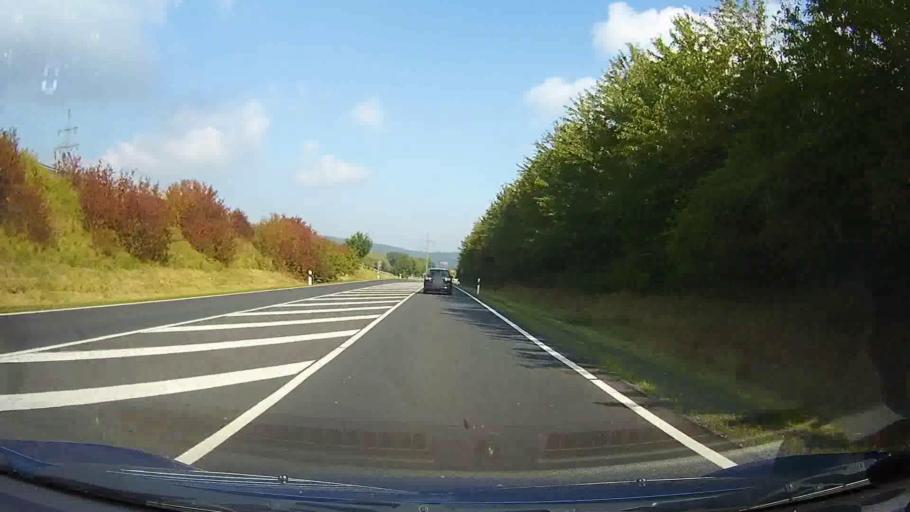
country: DE
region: Lower Saxony
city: Hardegsen
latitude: 51.6386
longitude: 9.8033
